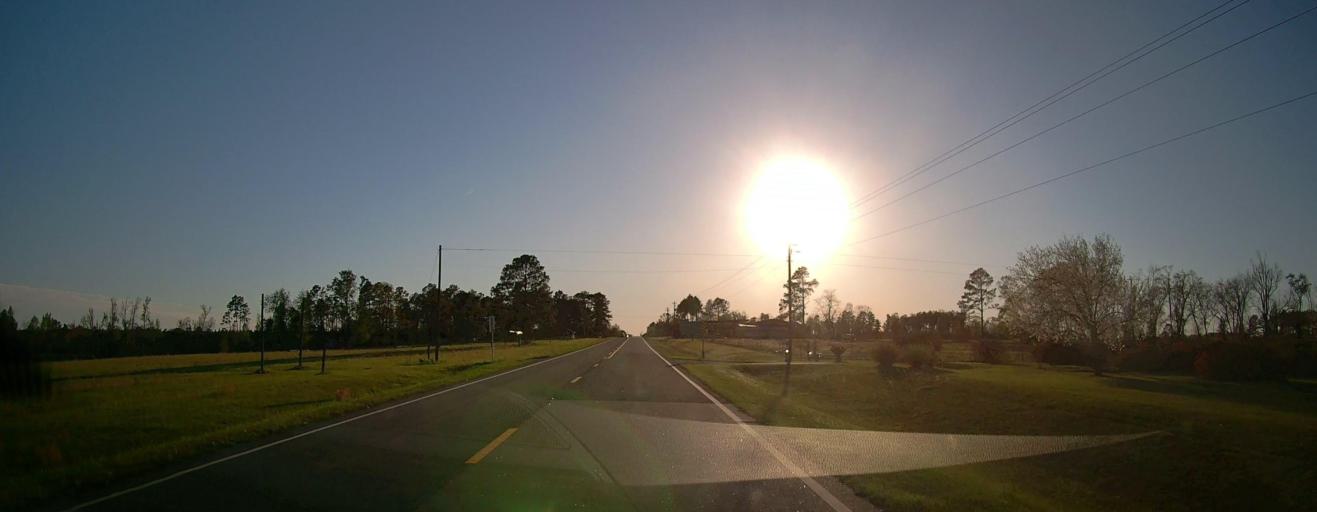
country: US
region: Georgia
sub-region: Wilcox County
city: Abbeville
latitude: 31.9705
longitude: -83.3737
